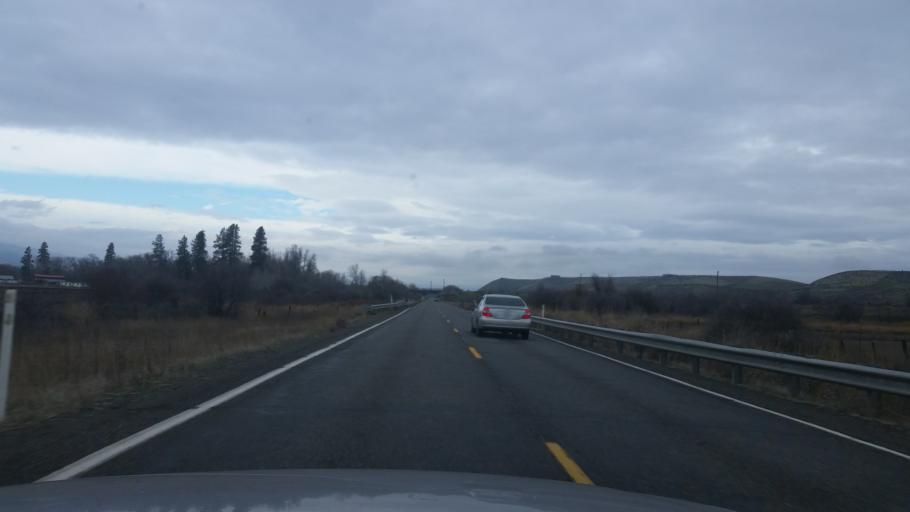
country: US
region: Washington
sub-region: Kittitas County
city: Ellensburg
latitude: 47.0377
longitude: -120.6154
